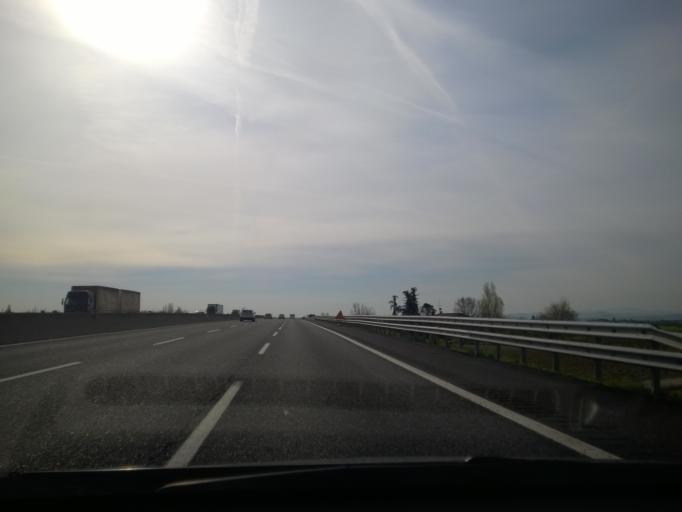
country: IT
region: Emilia-Romagna
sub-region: Forli-Cesena
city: Forlimpopoli
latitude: 44.2378
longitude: 12.1324
